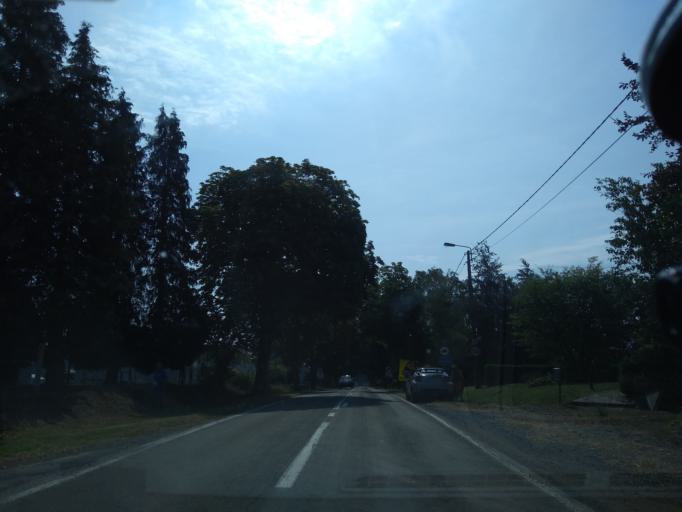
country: BE
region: Wallonia
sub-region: Province du Luxembourg
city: La Roche-en-Ardenne
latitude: 50.1663
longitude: 5.5559
